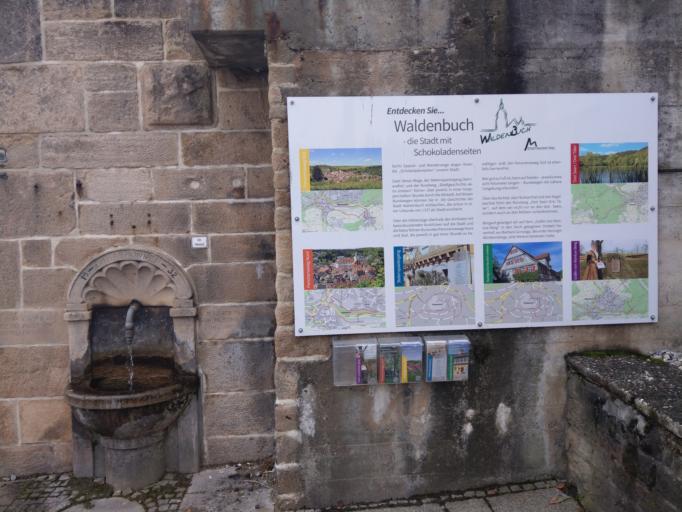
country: DE
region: Baden-Wuerttemberg
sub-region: Regierungsbezirk Stuttgart
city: Waldenbuch
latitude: 48.6365
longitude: 9.1285
